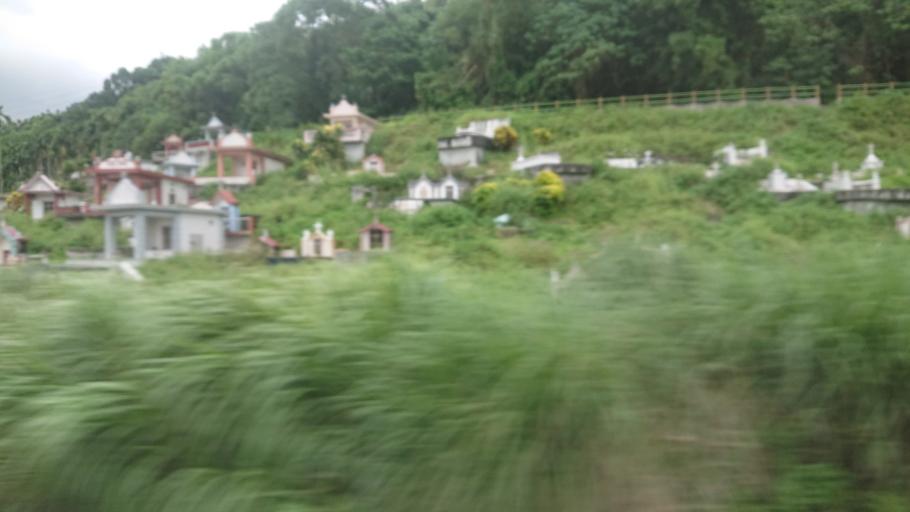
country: TW
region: Taiwan
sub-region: Hualien
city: Hualian
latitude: 23.5860
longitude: 121.3817
